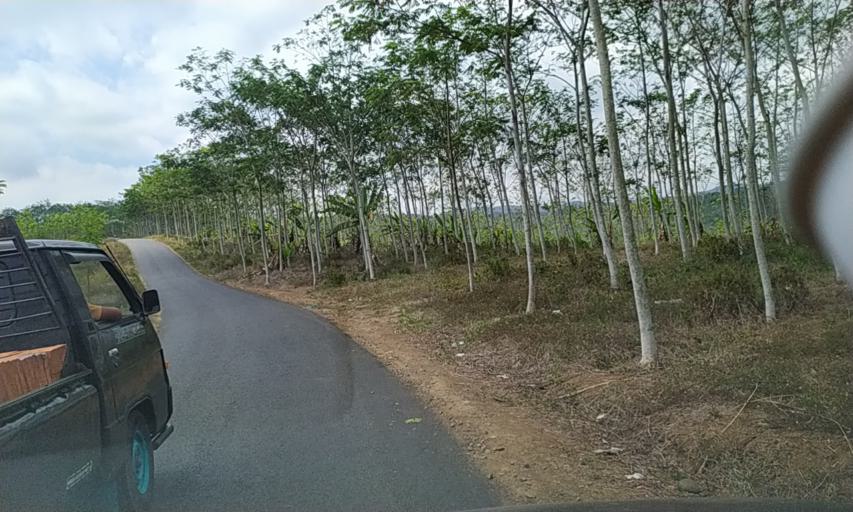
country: ID
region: Central Java
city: Cimalati
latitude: -7.2912
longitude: 108.6450
